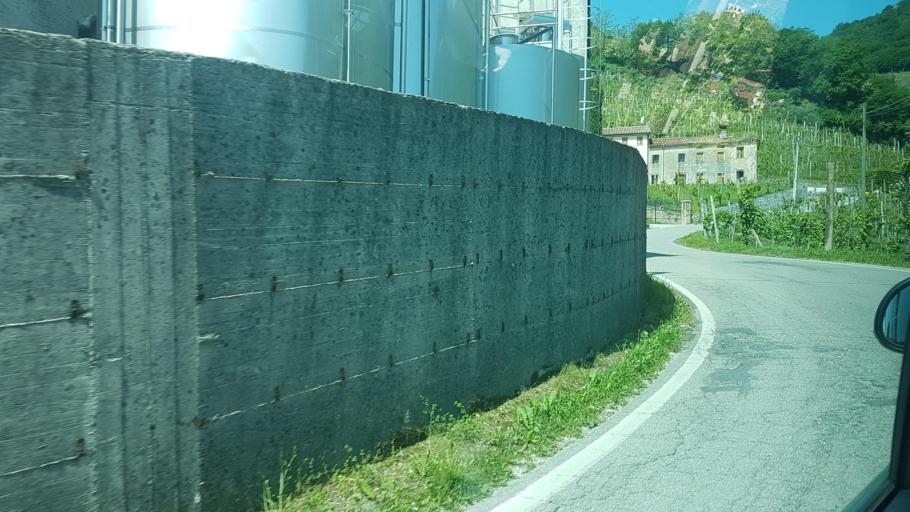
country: IT
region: Veneto
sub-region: Provincia di Treviso
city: Vidor
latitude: 45.9020
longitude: 12.0369
